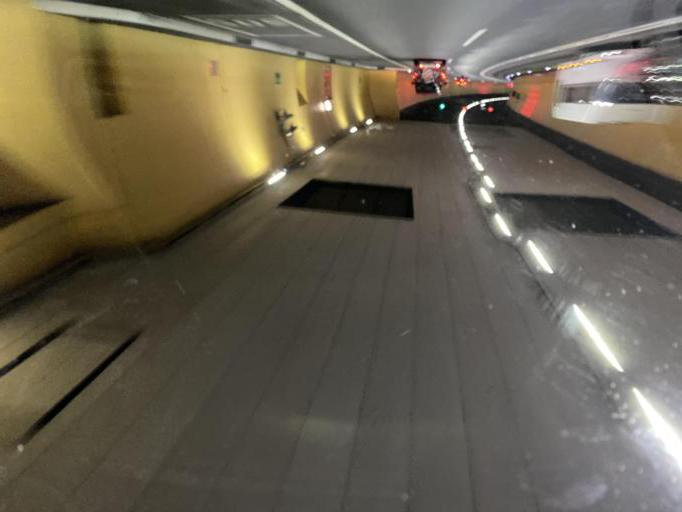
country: CH
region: Grisons
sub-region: Hinterrhein District
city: Thusis
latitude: 46.6907
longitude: 9.4389
